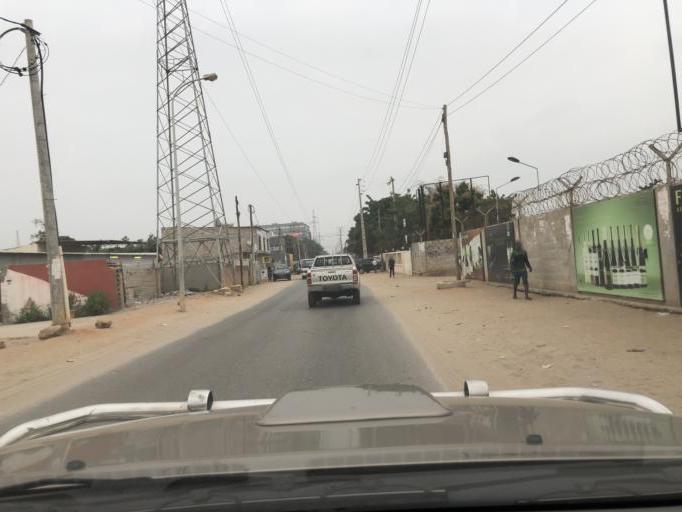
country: AO
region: Luanda
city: Luanda
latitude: -8.8868
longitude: 13.1868
